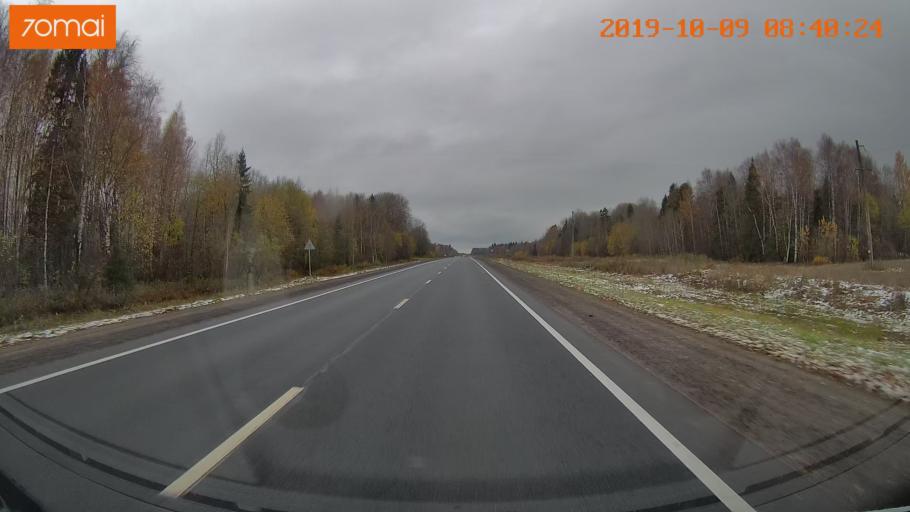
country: RU
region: Vologda
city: Gryazovets
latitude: 58.9860
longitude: 40.1408
